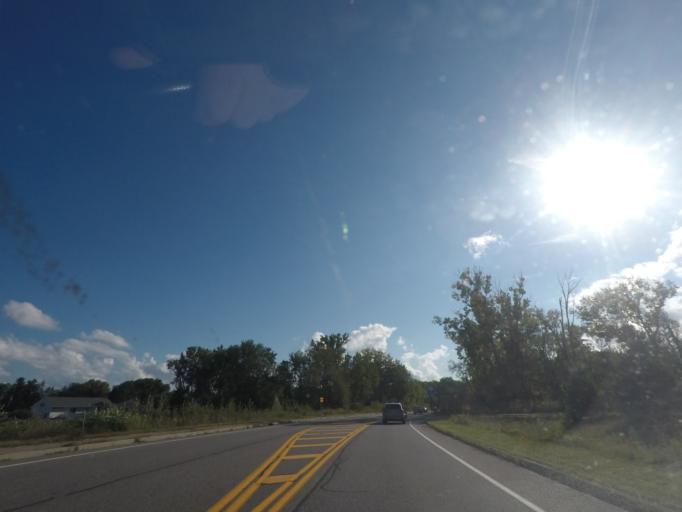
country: US
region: New York
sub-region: Albany County
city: Roessleville
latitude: 42.7254
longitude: -73.7891
